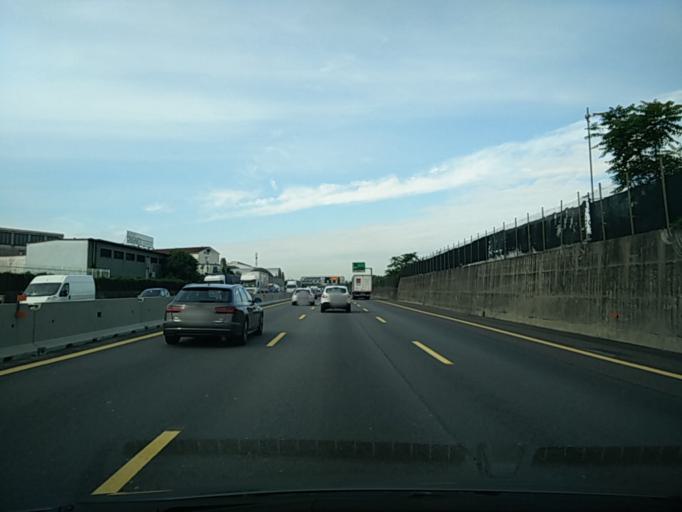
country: IT
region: Lombardy
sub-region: Citta metropolitana di Milano
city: Novate Milanese
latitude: 45.5326
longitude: 9.1550
